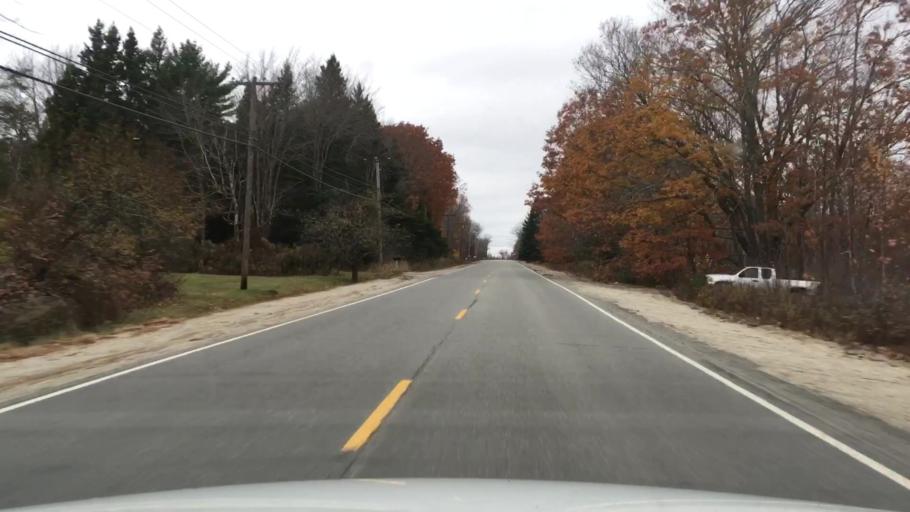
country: US
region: Maine
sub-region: Hancock County
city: Sedgwick
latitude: 44.3970
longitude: -68.5876
